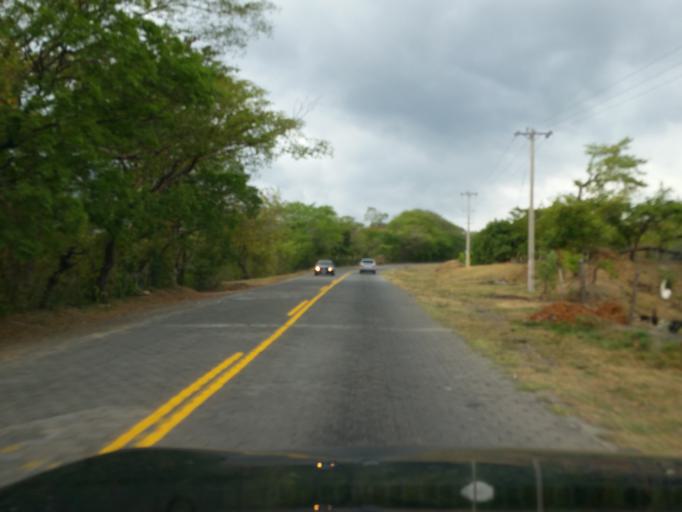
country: NI
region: Managua
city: San Rafael del Sur
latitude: 11.8763
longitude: -86.5153
